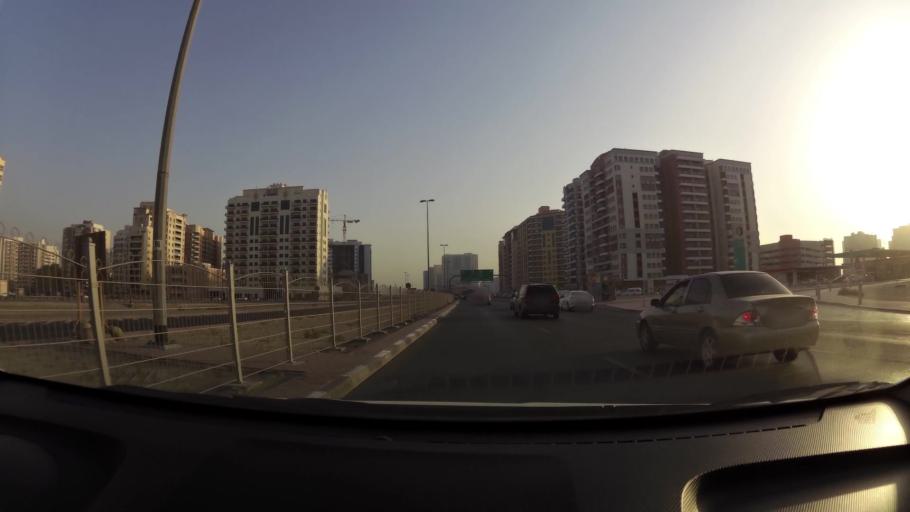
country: AE
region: Ash Shariqah
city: Sharjah
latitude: 25.2942
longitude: 55.3719
